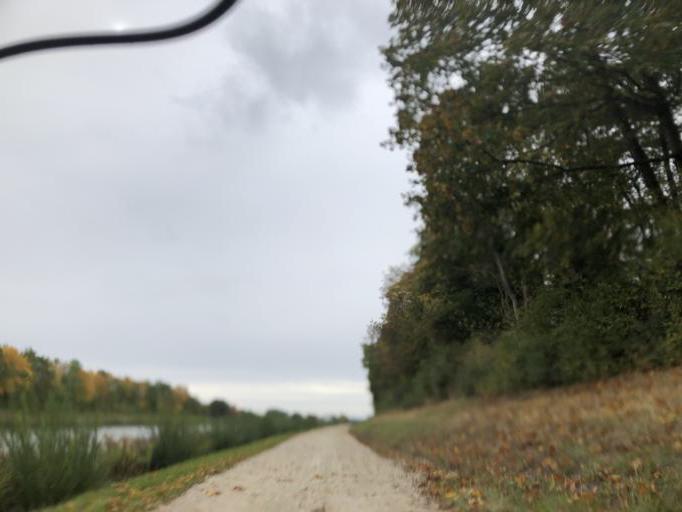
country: DE
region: Bavaria
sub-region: Regierungsbezirk Mittelfranken
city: Obermichelbach
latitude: 49.5351
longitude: 10.9662
